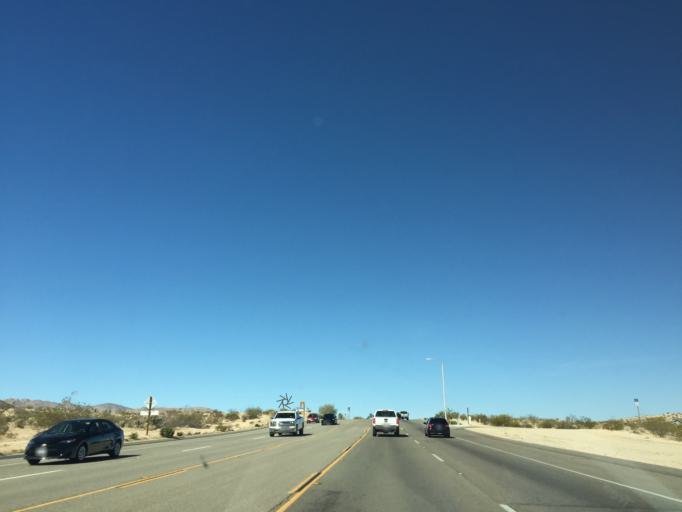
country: US
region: California
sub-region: San Bernardino County
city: Twentynine Palms
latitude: 34.1353
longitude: -116.1102
